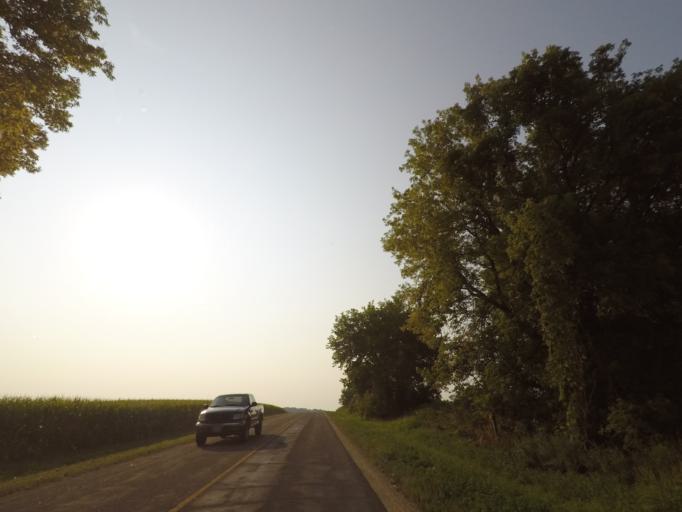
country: US
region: Wisconsin
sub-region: Dane County
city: Cottage Grove
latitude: 43.0481
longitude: -89.2397
